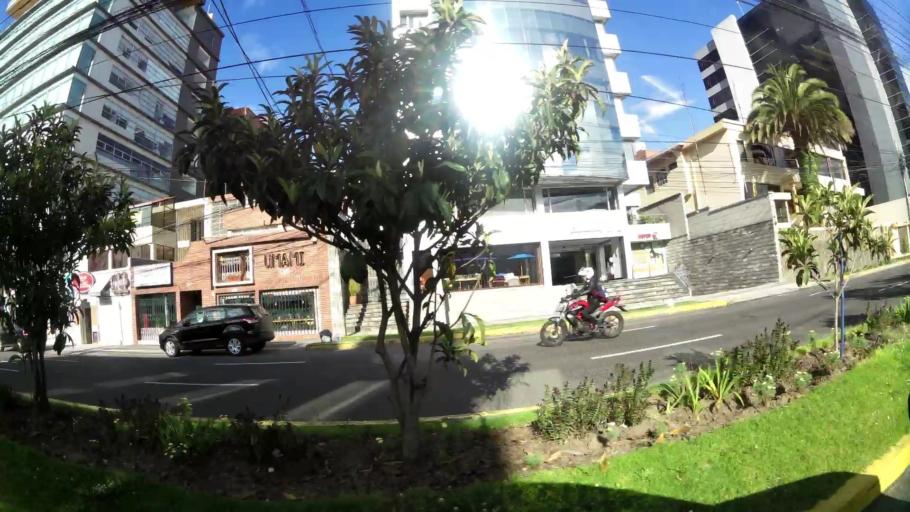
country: EC
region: Pichincha
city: Quito
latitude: -0.1991
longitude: -78.4824
